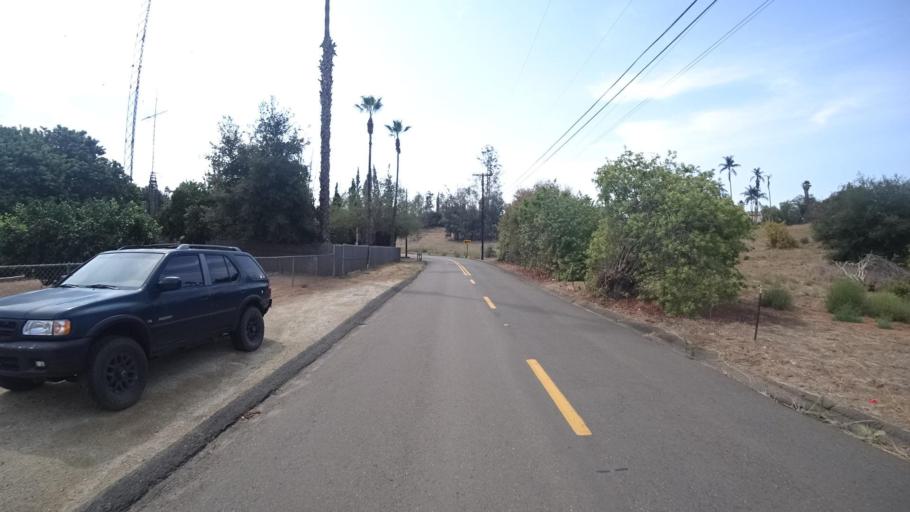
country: US
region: California
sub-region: San Diego County
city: Escondido
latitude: 33.1102
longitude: -117.0430
